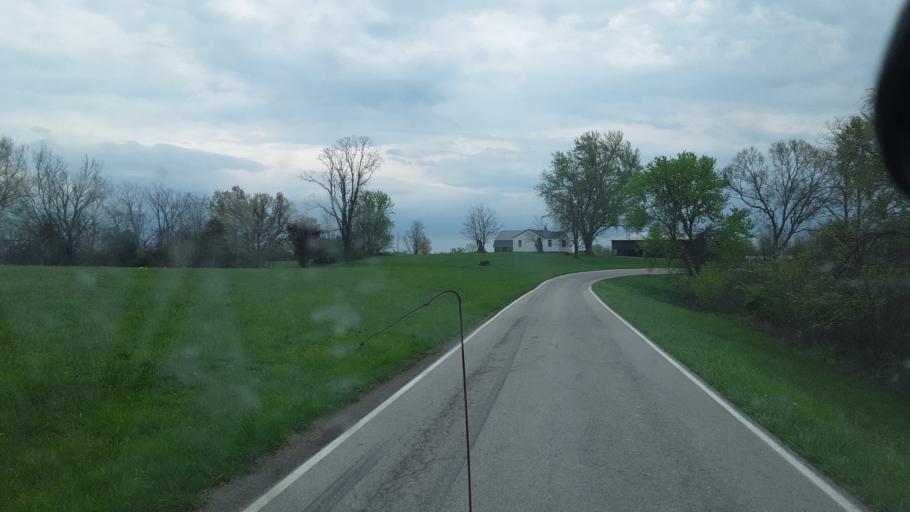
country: US
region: Kentucky
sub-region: Owen County
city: Owenton
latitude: 38.6549
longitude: -84.7716
